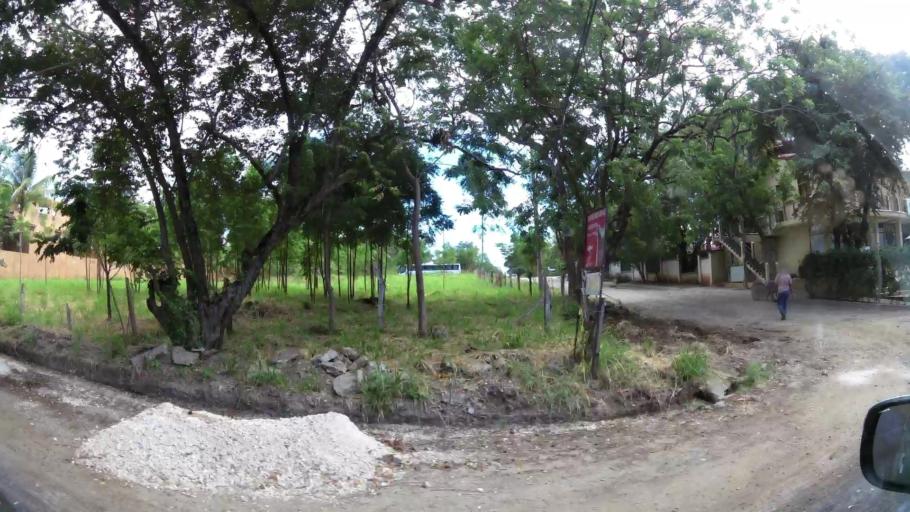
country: CR
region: Guanacaste
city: Santa Cruz
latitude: 10.2878
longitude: -85.8507
